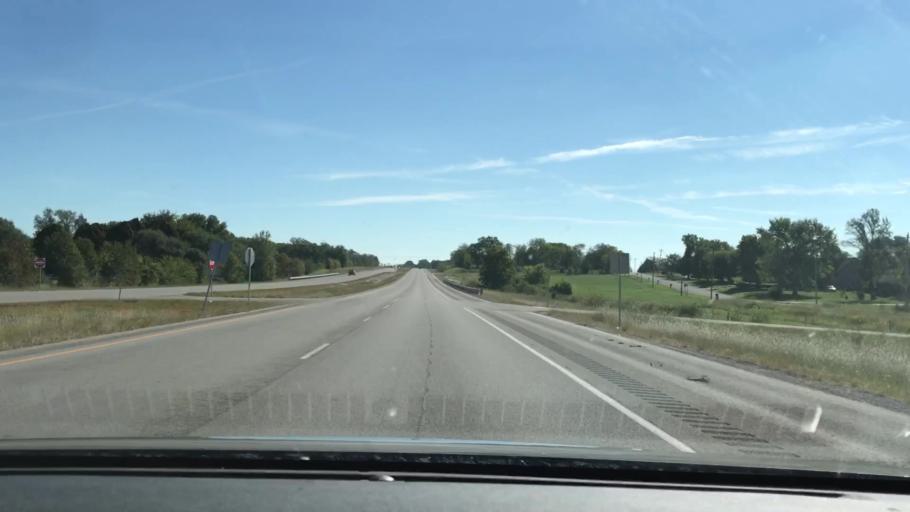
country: US
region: Kentucky
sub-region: Christian County
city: Hopkinsville
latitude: 36.8559
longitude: -87.4193
